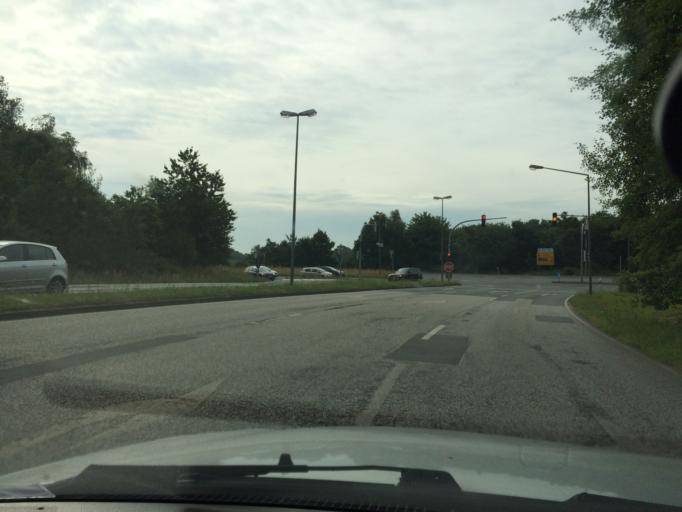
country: DE
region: Schleswig-Holstein
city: Flensburg
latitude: 54.7584
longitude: 9.4404
